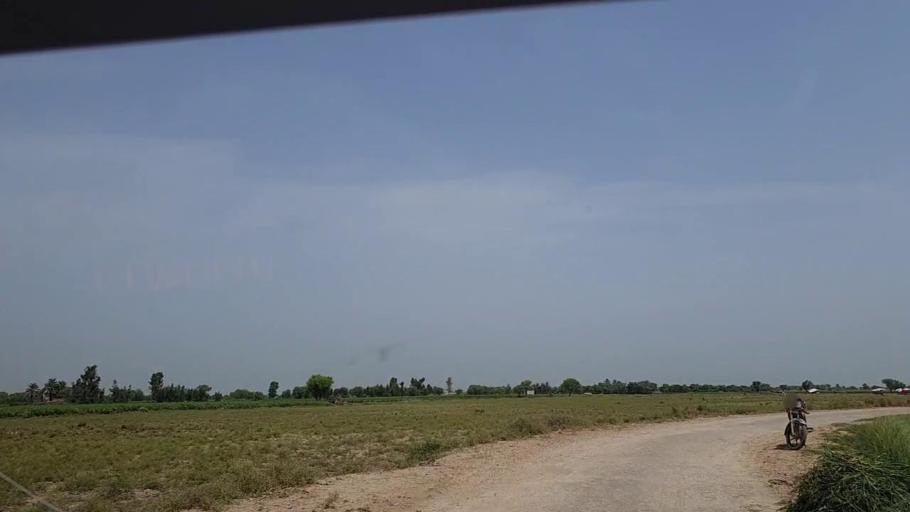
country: PK
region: Sindh
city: Tharu Shah
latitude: 26.9125
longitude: 68.0530
